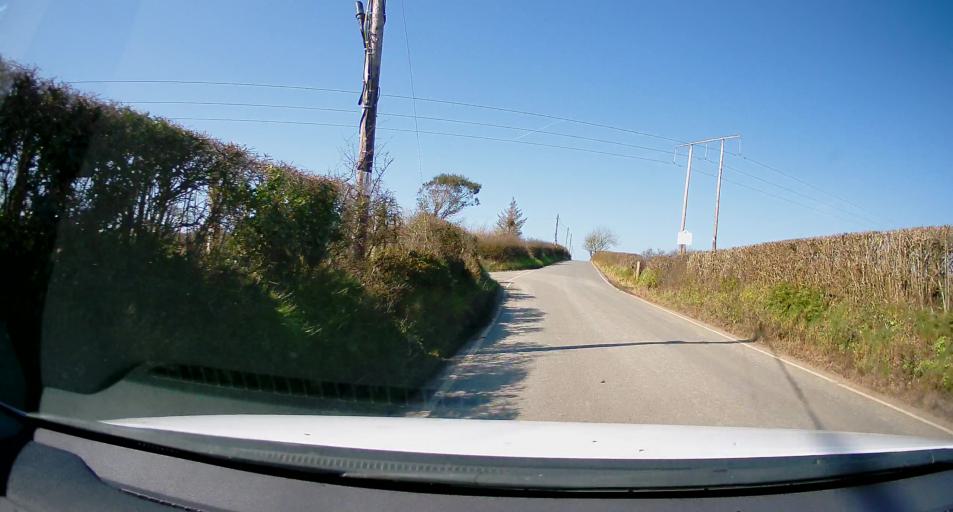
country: GB
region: Wales
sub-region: County of Ceredigion
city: Penparcau
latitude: 52.3210
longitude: -4.0652
